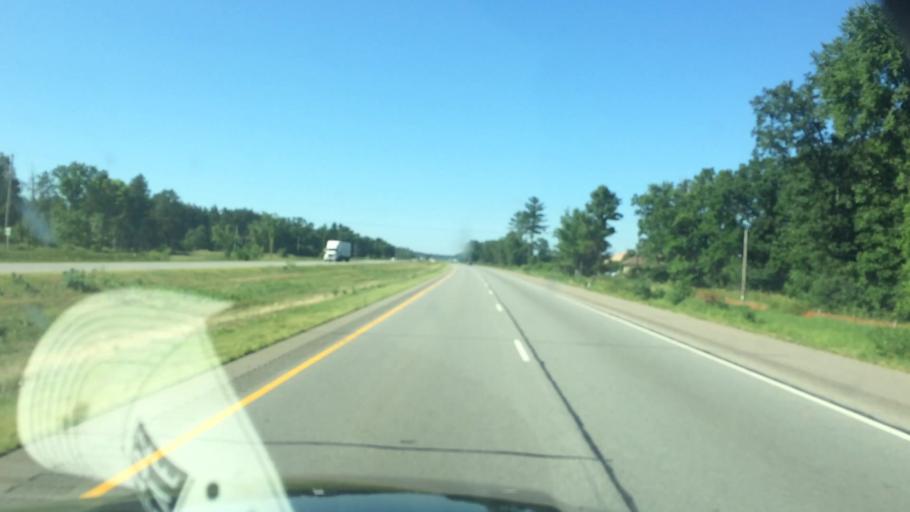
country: US
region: Wisconsin
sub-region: Marathon County
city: Evergreen
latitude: 44.8380
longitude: -89.6515
